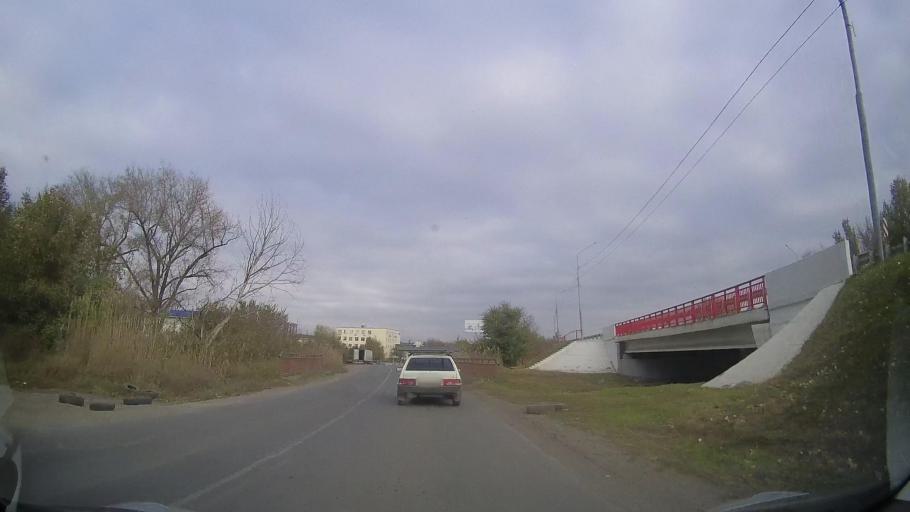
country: RU
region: Rostov
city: Bataysk
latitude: 47.0961
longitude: 39.7635
